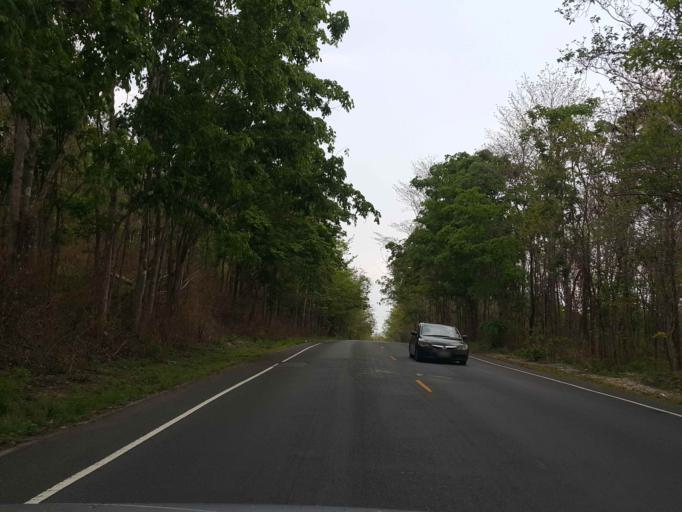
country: TH
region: Sukhothai
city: Thung Saliam
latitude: 17.4046
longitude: 99.3902
